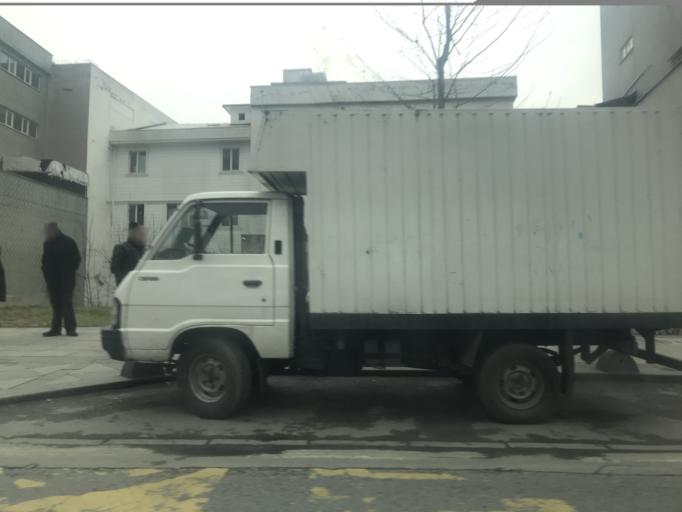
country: TR
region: Istanbul
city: Mahmutbey
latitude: 41.0439
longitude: 28.8311
